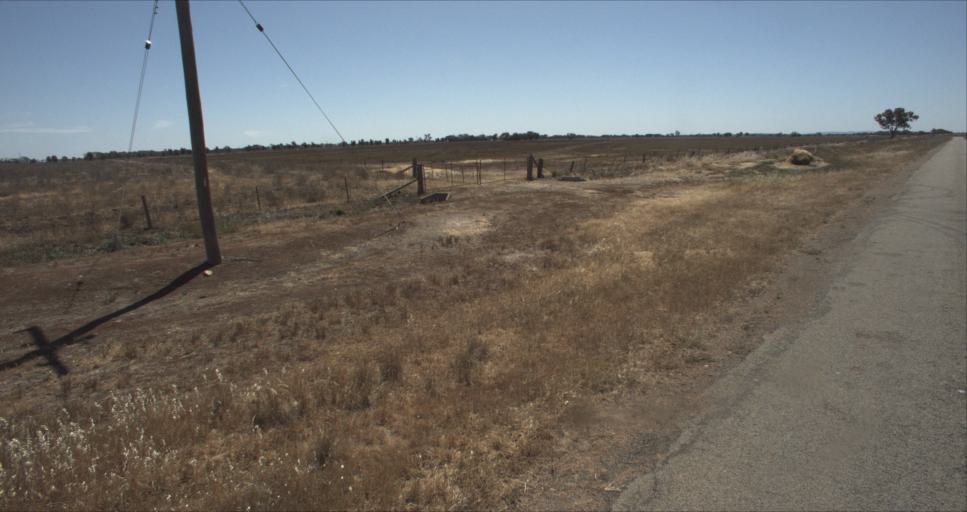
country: AU
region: New South Wales
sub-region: Leeton
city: Leeton
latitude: -34.5049
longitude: 146.3443
